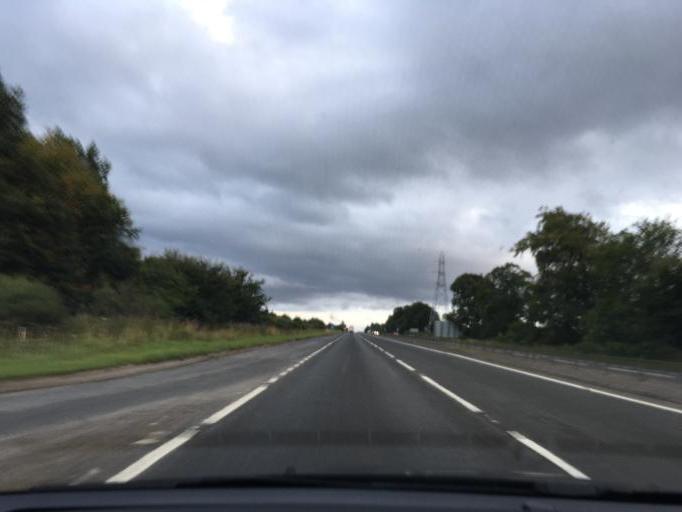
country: GB
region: Scotland
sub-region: Highland
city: Inverness
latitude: 57.4518
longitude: -4.1588
